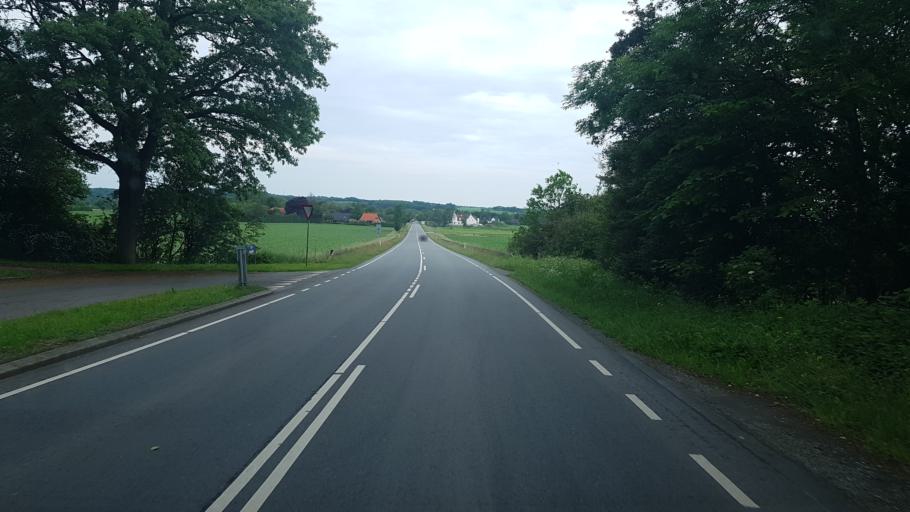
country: DK
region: South Denmark
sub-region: Vejen Kommune
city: Brorup
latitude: 55.4355
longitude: 9.0095
